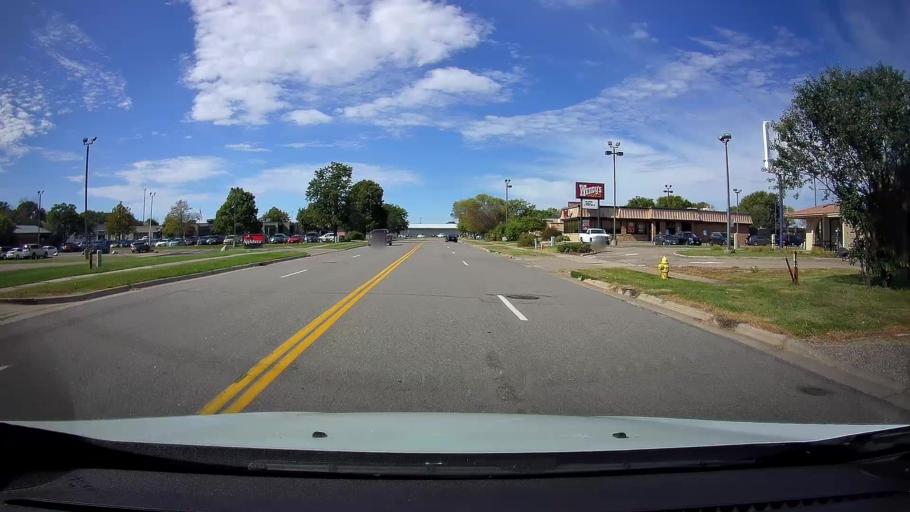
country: US
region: Minnesota
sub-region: Ramsey County
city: Roseville
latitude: 45.0119
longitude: -93.1793
